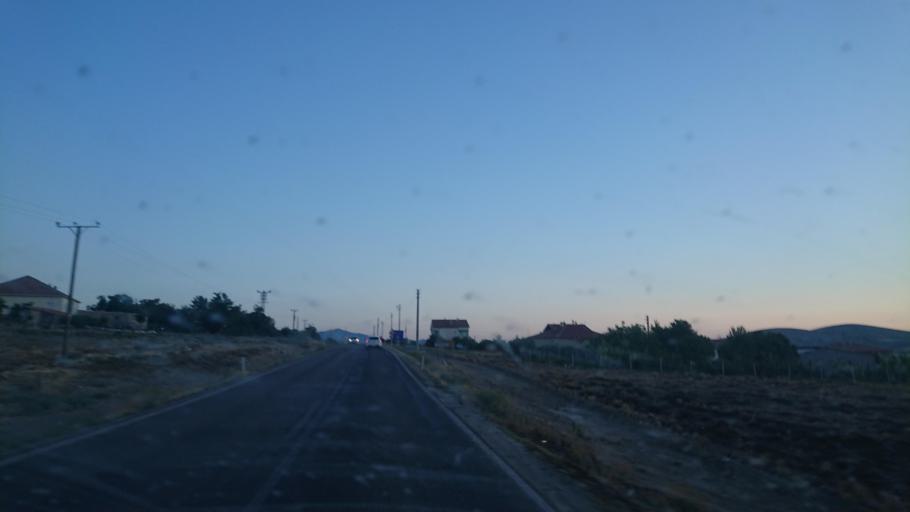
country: TR
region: Aksaray
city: Balci
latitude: 38.7968
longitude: 34.1270
